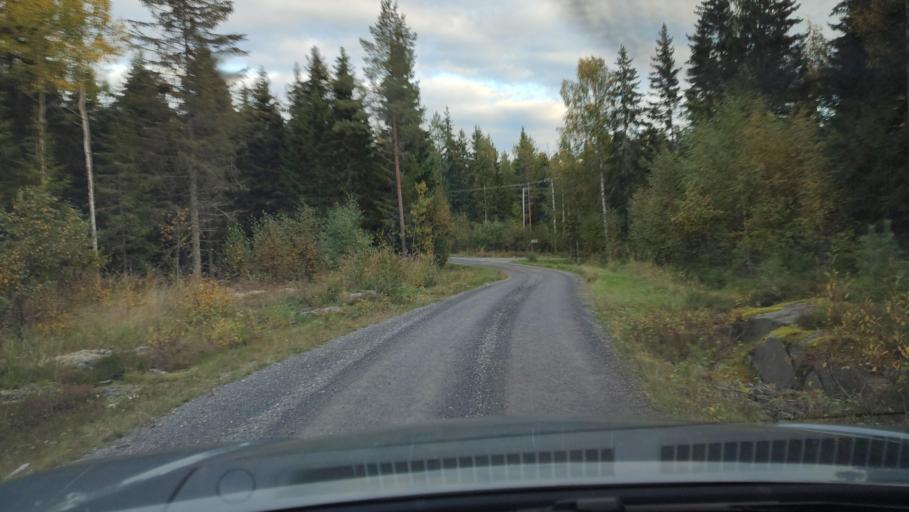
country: FI
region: Ostrobothnia
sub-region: Sydosterbotten
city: Kristinestad
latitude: 62.2304
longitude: 21.4204
